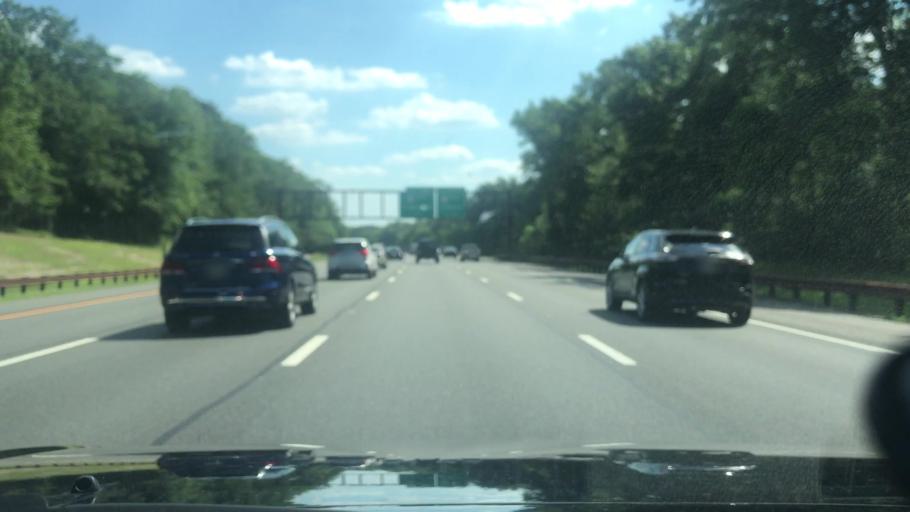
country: US
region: New Jersey
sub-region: Monmouth County
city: Shark River Hills
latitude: 40.2296
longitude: -74.0962
